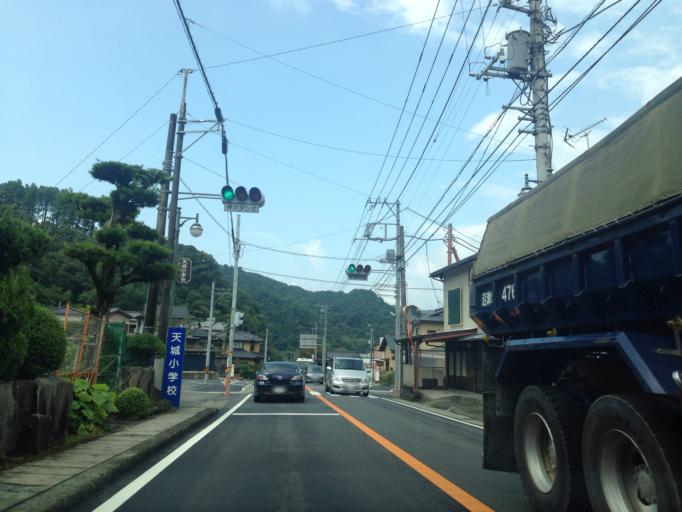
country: JP
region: Shizuoka
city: Heda
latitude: 34.9367
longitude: 138.9321
